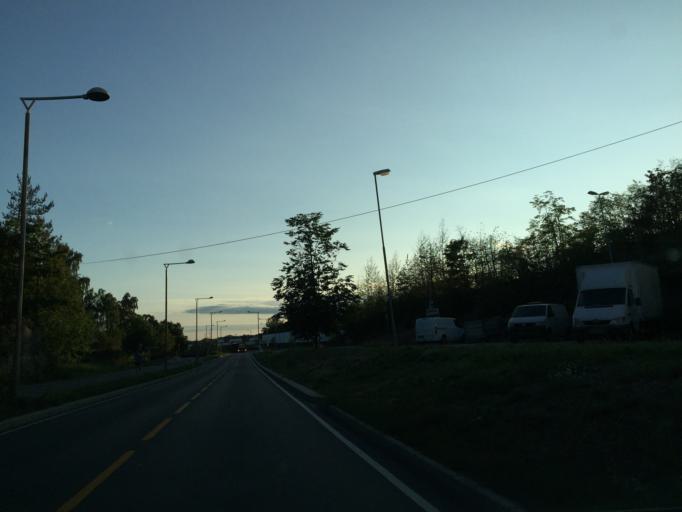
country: NO
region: Akershus
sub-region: Baerum
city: Lysaker
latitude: 59.8913
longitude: 10.6258
